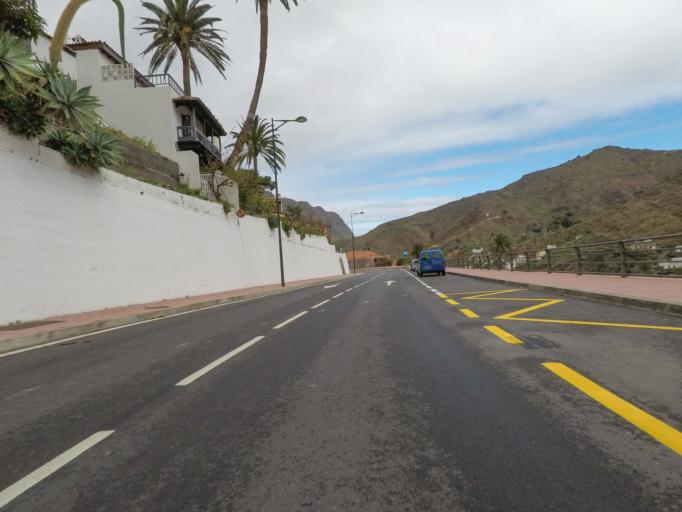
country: ES
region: Canary Islands
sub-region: Provincia de Santa Cruz de Tenerife
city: Hermigua
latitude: 28.1518
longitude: -17.1981
